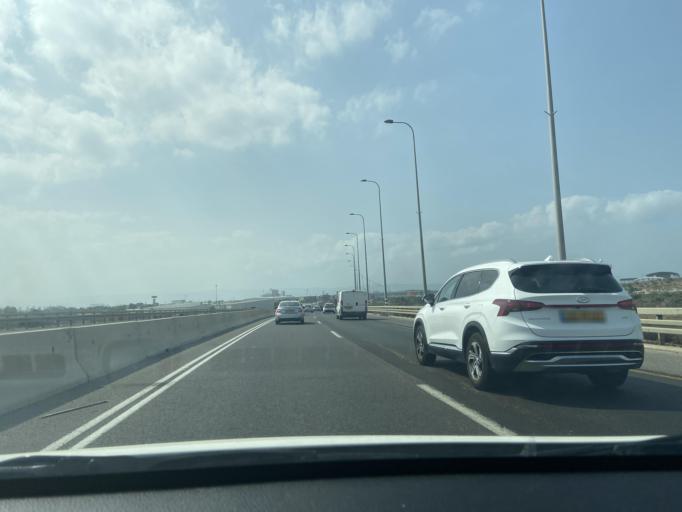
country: IL
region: Northern District
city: `Akko
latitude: 32.9110
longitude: 35.0952
